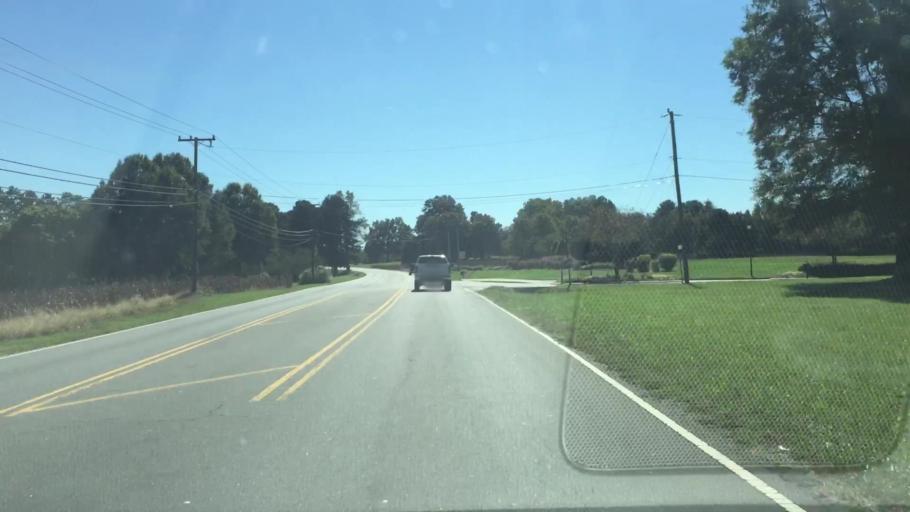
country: US
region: North Carolina
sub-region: Rowan County
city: Enochville
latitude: 35.4475
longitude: -80.7305
